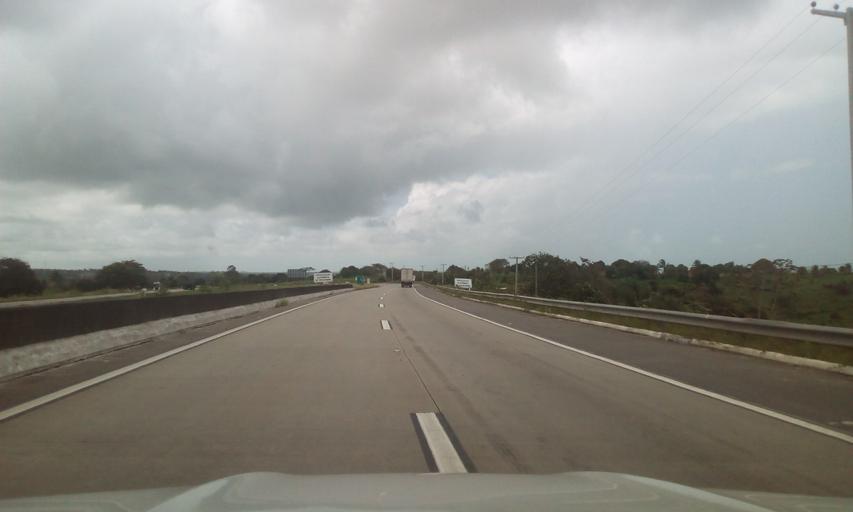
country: BR
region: Pernambuco
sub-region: Itapissuma
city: Itapissuma
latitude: -7.7041
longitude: -34.9248
